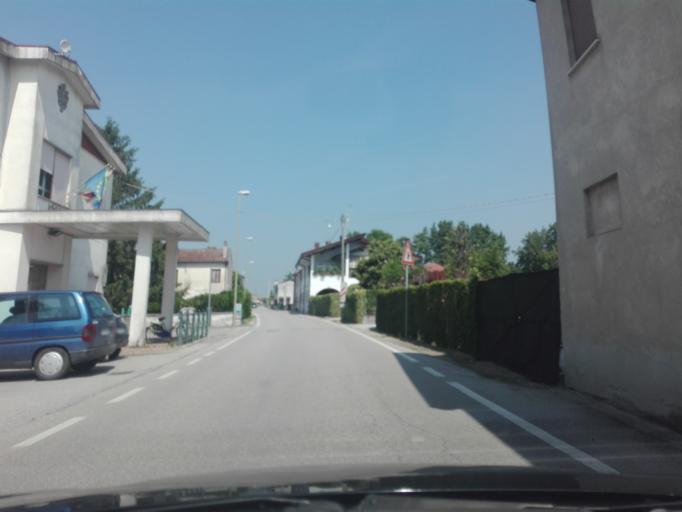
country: IT
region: Veneto
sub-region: Provincia di Rovigo
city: Adria
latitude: 45.0595
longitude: 11.9953
